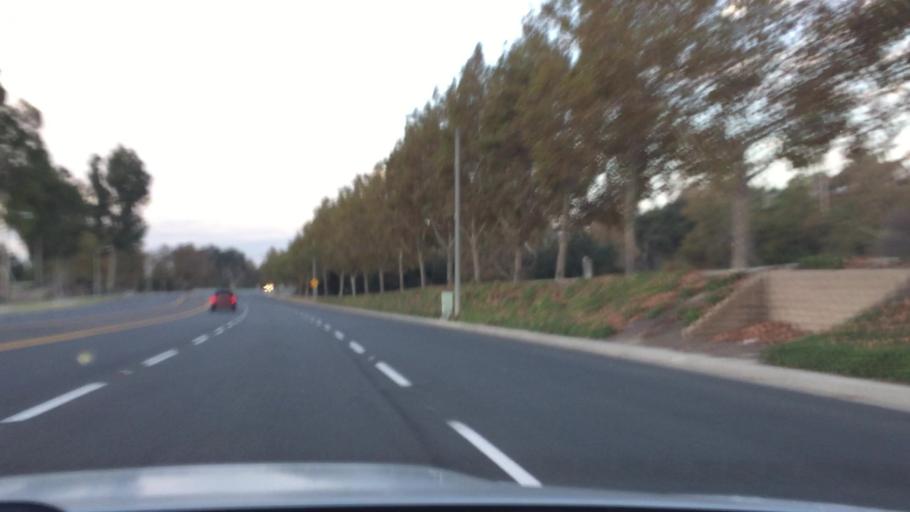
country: US
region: California
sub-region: Orange County
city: Lake Forest
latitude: 33.6466
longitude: -117.6638
